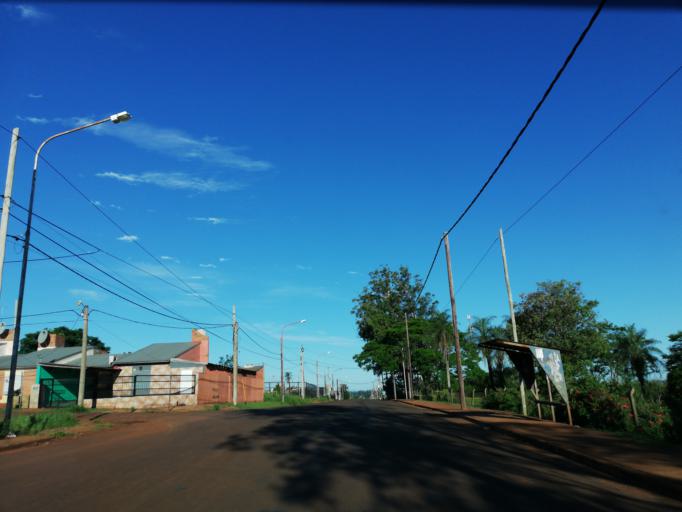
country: AR
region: Misiones
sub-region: Departamento de Capital
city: Posadas
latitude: -27.4342
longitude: -55.9304
